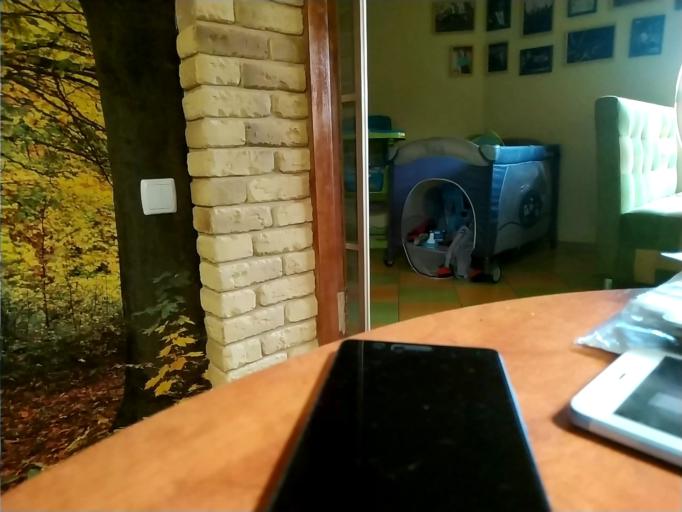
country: RU
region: Kaluga
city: Duminichi
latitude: 53.7236
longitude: 35.4224
